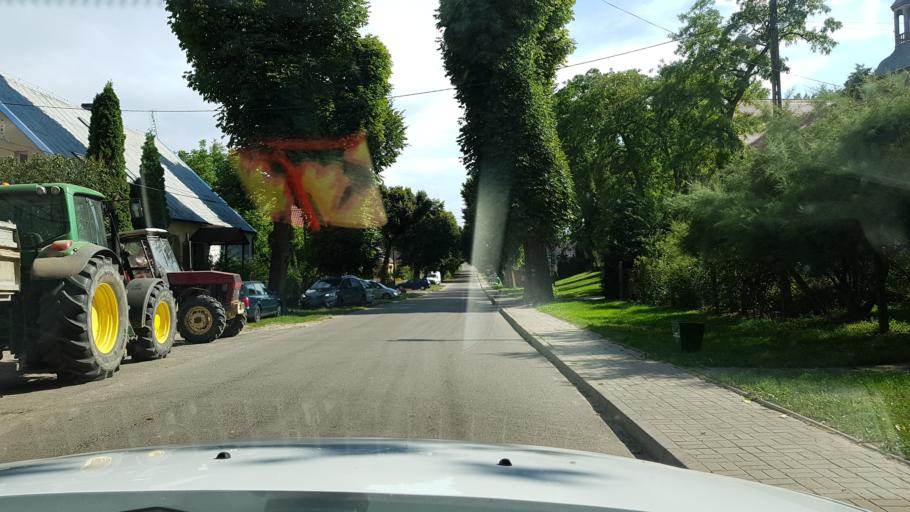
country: PL
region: West Pomeranian Voivodeship
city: Trzcinsko Zdroj
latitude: 52.9539
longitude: 14.5491
